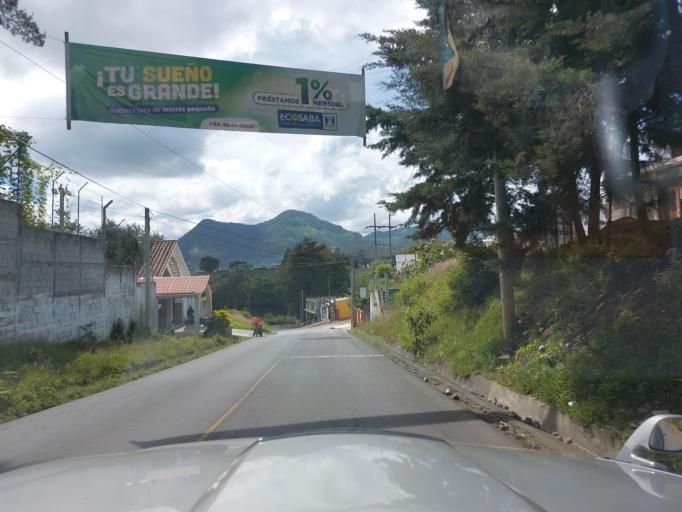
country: GT
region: Chimaltenango
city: Parramos
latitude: 14.6089
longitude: -90.8103
